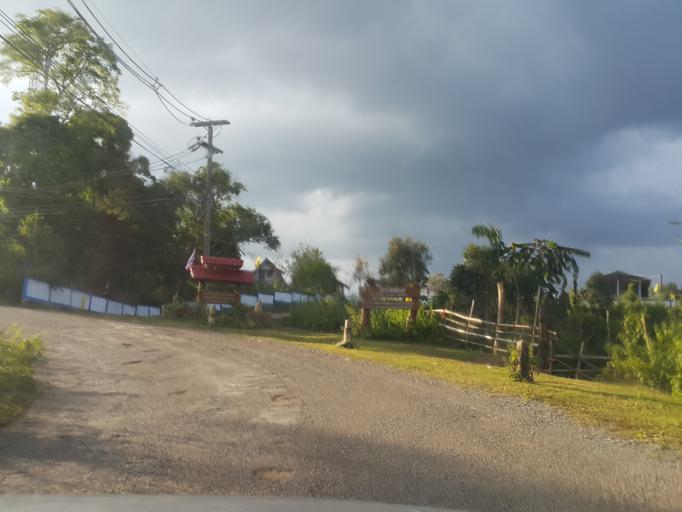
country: TH
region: Chiang Mai
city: Mae Chaem
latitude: 18.7454
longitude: 98.2157
